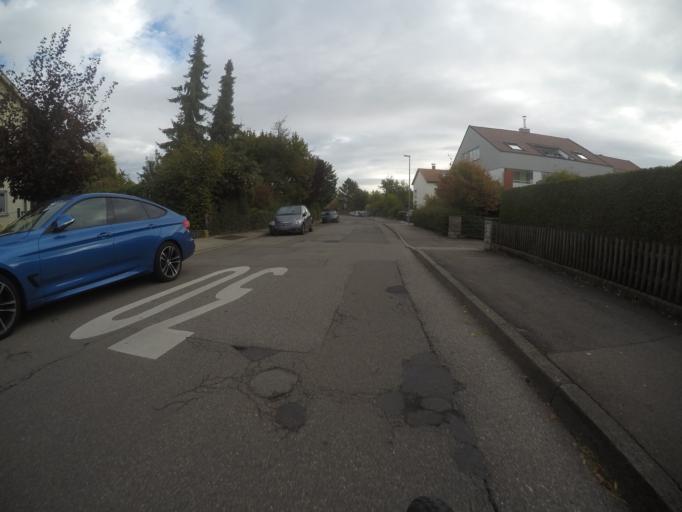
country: DE
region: Baden-Wuerttemberg
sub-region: Regierungsbezirk Stuttgart
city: Leinfelden-Echterdingen
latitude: 48.7359
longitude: 9.1198
